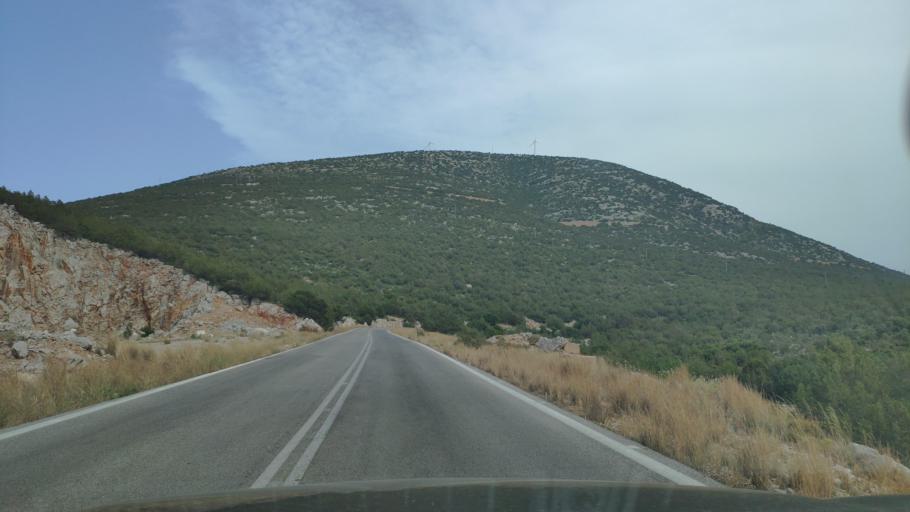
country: GR
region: Peloponnese
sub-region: Nomos Argolidos
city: Didyma
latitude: 37.5044
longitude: 23.1904
